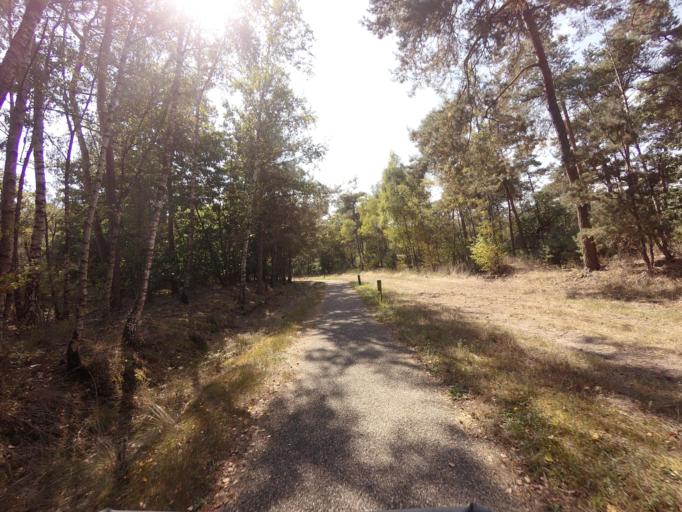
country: NL
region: North Brabant
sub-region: Gemeente Someren
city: Someren
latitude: 51.3645
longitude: 5.6575
